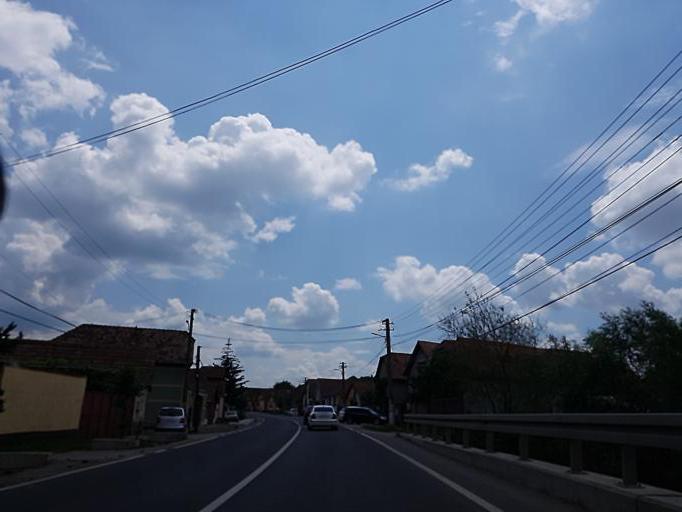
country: RO
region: Sibiu
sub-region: Comuna Slimnic
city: Slimnic
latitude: 45.9129
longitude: 24.1539
